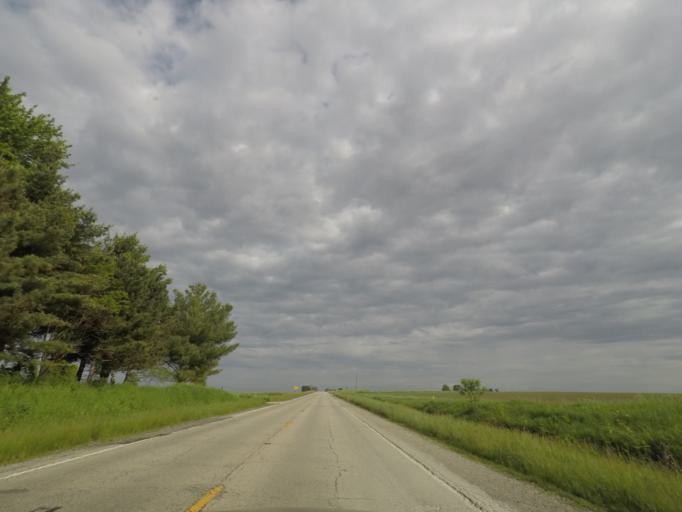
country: US
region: Illinois
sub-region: Logan County
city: Mount Pulaski
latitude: 40.0693
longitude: -89.2906
